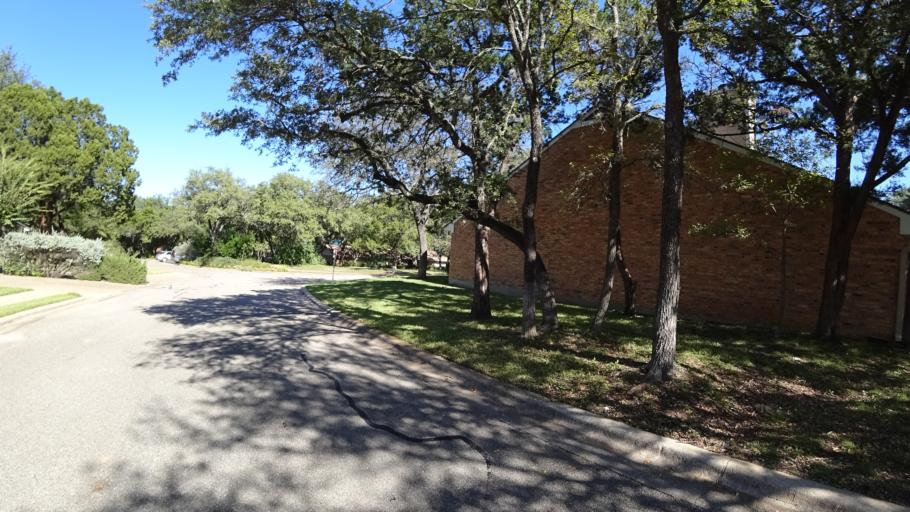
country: US
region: Texas
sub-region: Williamson County
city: Jollyville
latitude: 30.3660
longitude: -97.7551
